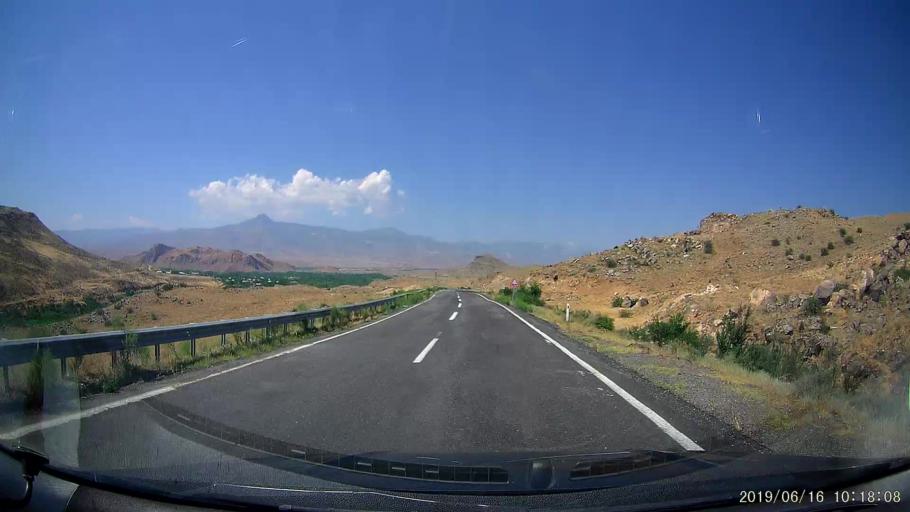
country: TR
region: Igdir
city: Tuzluca
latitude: 40.1632
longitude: 43.6721
